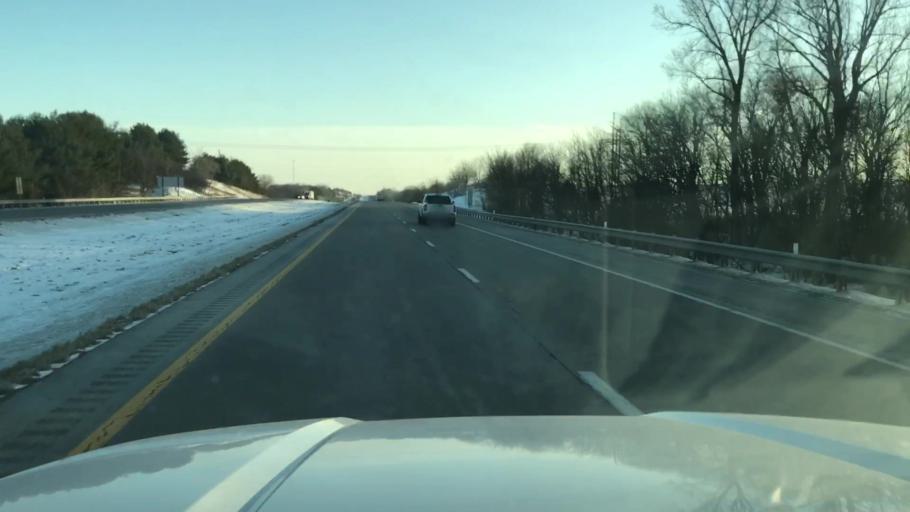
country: US
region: Missouri
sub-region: Andrew County
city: Country Club Village
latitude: 39.8466
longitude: -94.8054
